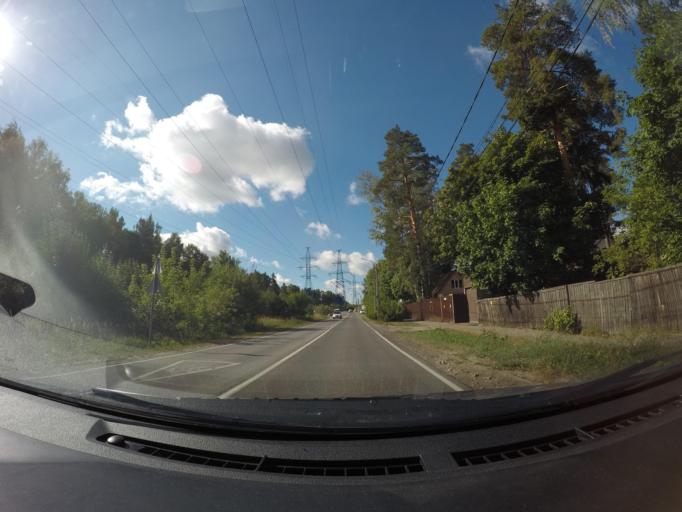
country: RU
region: Moskovskaya
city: Zhukovskiy
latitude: 55.6074
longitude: 38.1340
